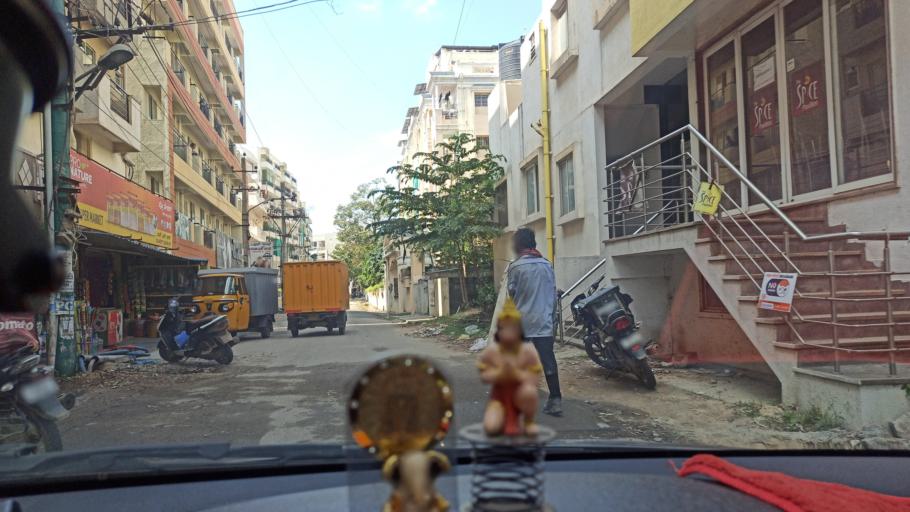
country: IN
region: Karnataka
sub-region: Bangalore Urban
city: Bangalore
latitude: 12.9777
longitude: 77.6932
